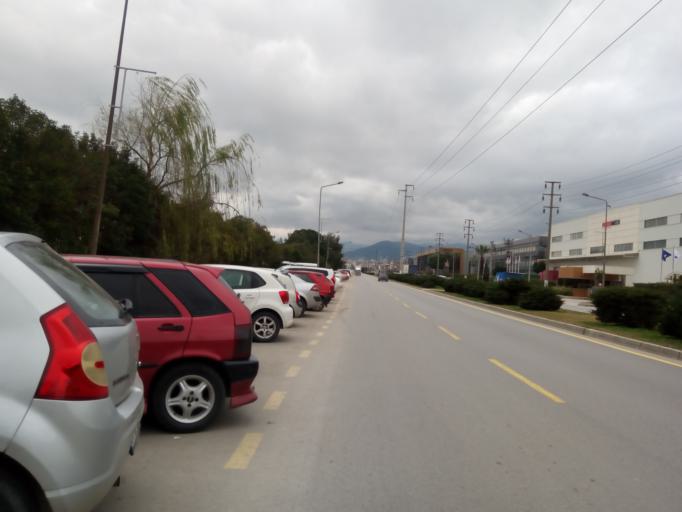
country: TR
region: Bursa
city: Niluefer
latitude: 40.2472
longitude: 28.9563
